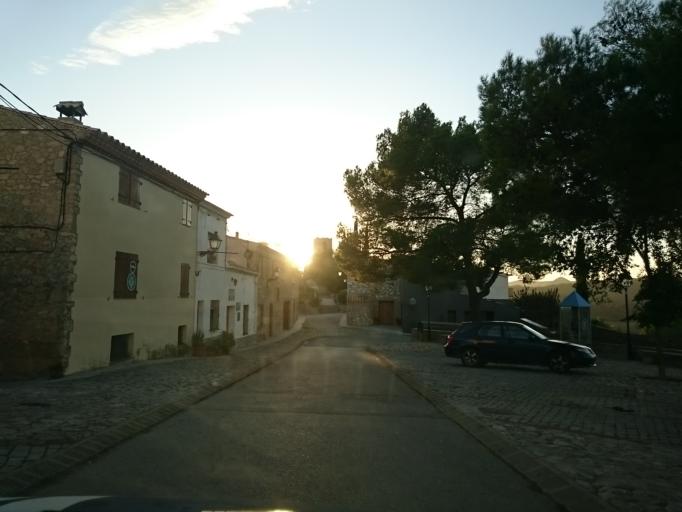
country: ES
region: Catalonia
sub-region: Provincia de Barcelona
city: Olivella
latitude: 41.3104
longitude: 1.8120
